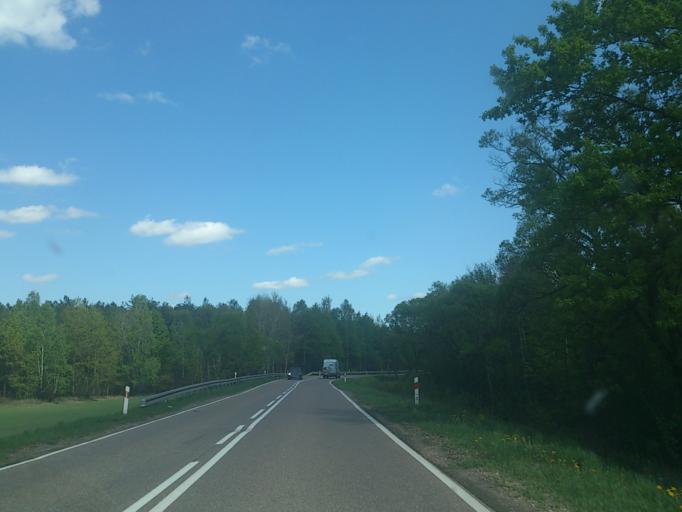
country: PL
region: Podlasie
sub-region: Powiat lomzynski
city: Wizna
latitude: 53.2016
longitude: 22.4306
